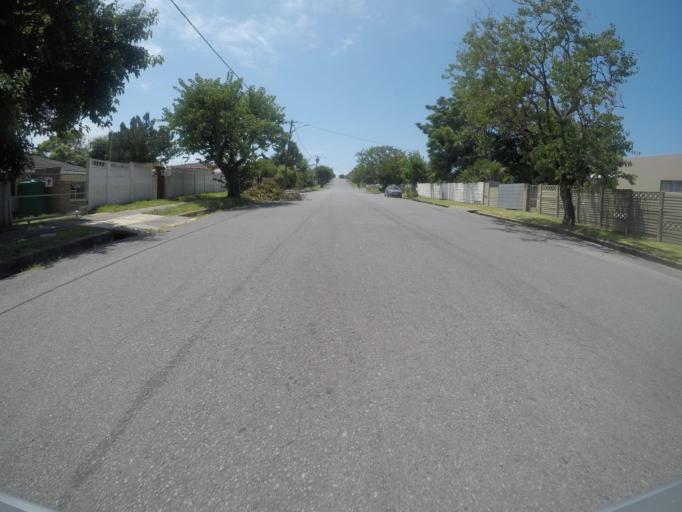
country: ZA
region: Eastern Cape
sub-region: Buffalo City Metropolitan Municipality
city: East London
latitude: -32.9786
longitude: 27.8795
